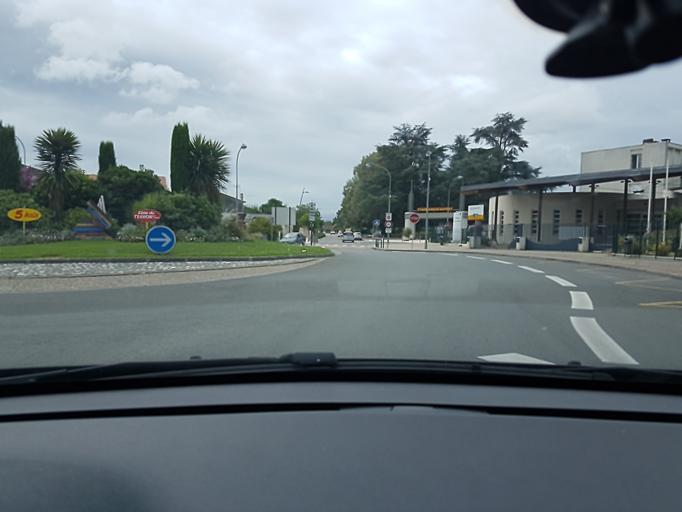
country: FR
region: Aquitaine
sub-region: Departement du Lot-et-Garonne
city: Nerac
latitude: 44.1410
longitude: 0.3341
